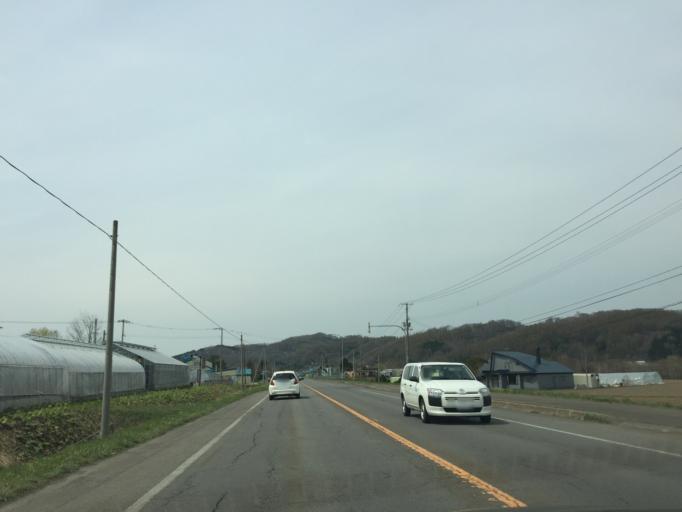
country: JP
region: Hokkaido
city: Ashibetsu
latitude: 43.5407
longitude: 142.1354
